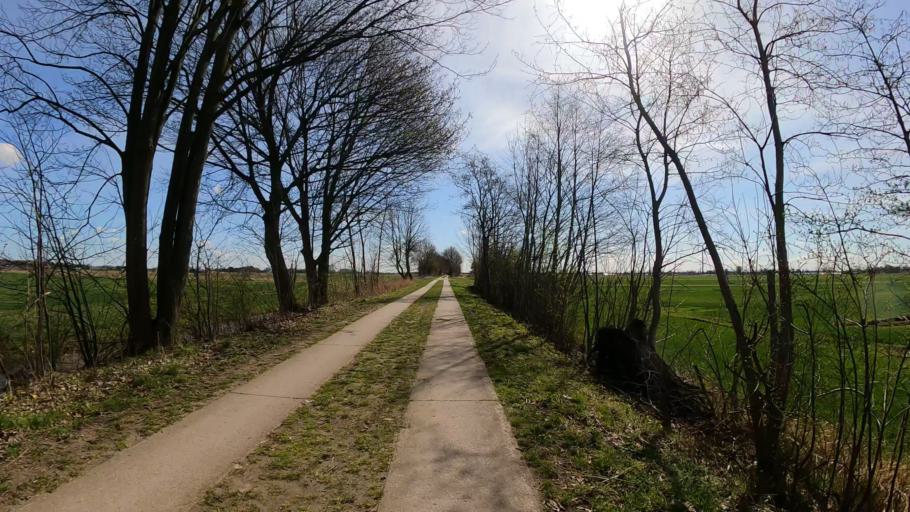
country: DE
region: Hamburg
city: Rothenburgsort
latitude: 53.4706
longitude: 10.0888
